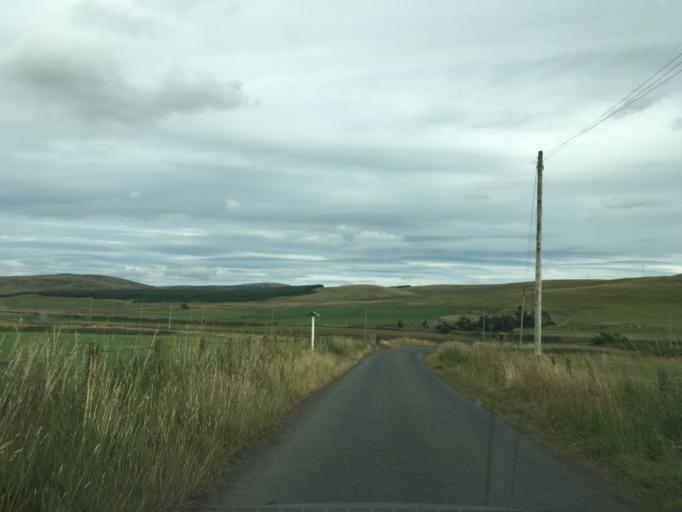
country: GB
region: Scotland
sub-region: South Lanarkshire
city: Douglas
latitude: 55.5182
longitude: -3.6895
